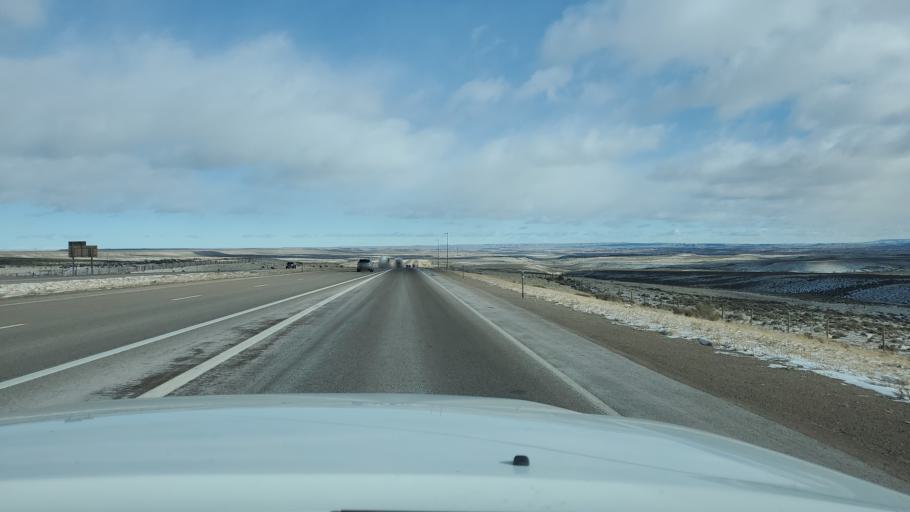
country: US
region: Wyoming
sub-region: Uinta County
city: Mountain View
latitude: 41.3135
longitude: -110.5049
